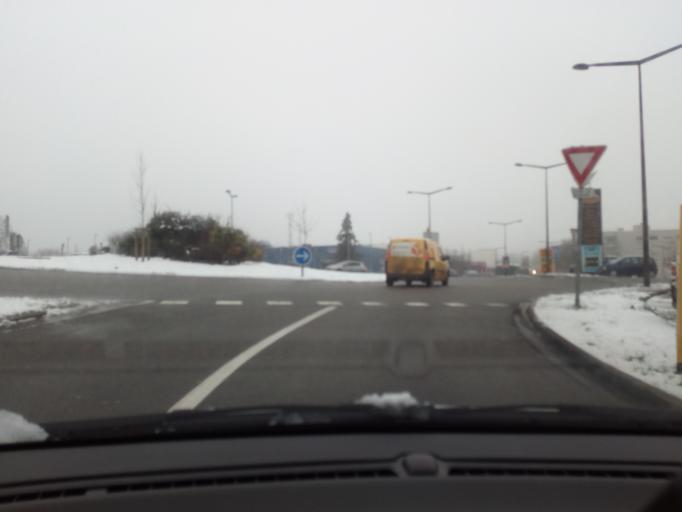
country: FR
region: Nord-Pas-de-Calais
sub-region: Departement du Nord
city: Maubeuge
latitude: 50.2727
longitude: 3.9736
